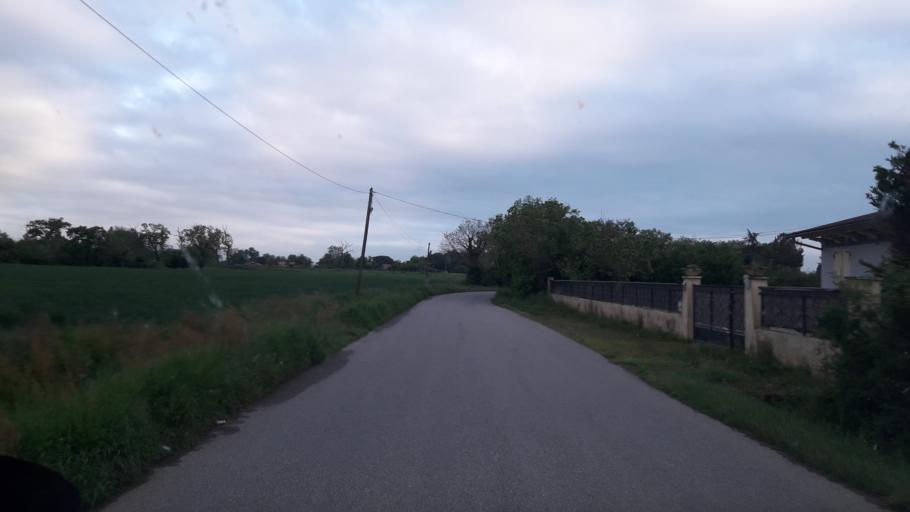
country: FR
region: Midi-Pyrenees
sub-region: Departement de la Haute-Garonne
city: Cazeres
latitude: 43.2221
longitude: 1.0831
